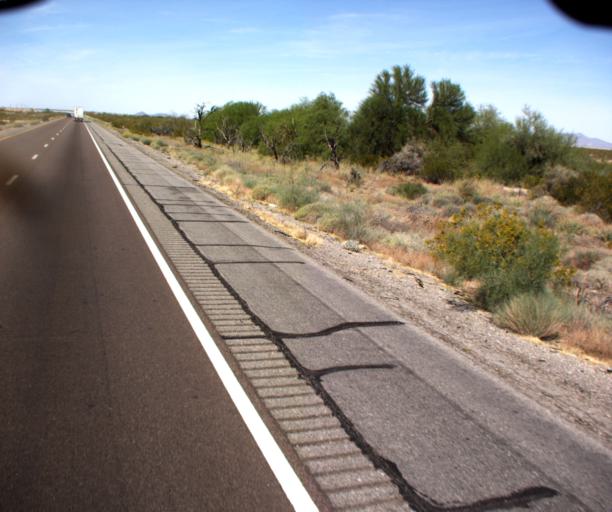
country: US
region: Arizona
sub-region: La Paz County
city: Salome
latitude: 33.5592
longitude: -113.2864
